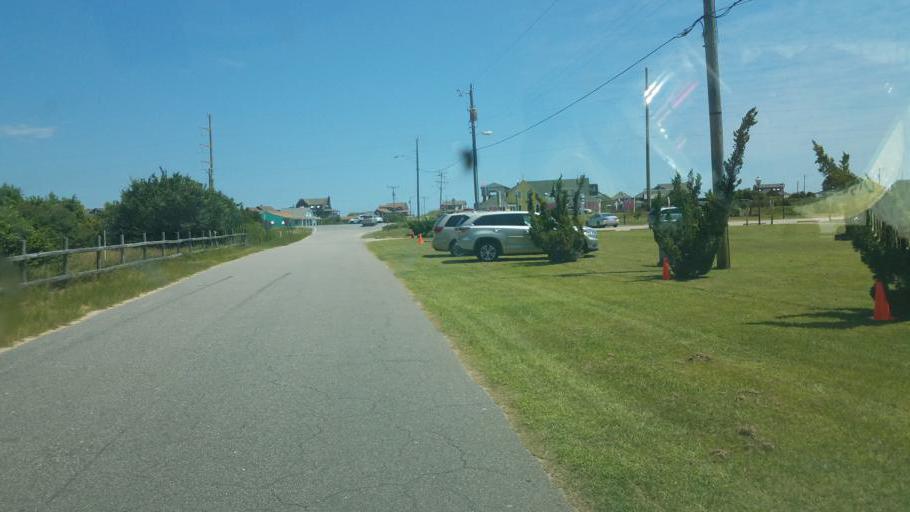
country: US
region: North Carolina
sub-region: Dare County
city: Nags Head
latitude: 35.9558
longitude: -75.6265
